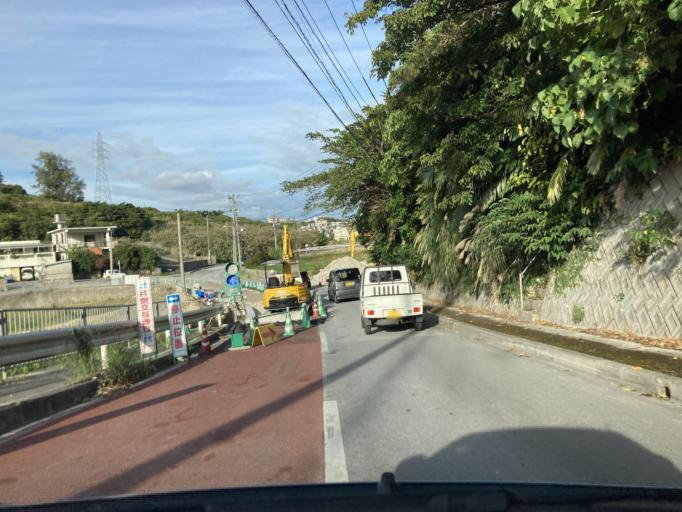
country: JP
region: Okinawa
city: Tomigusuku
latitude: 26.1594
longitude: 127.7373
